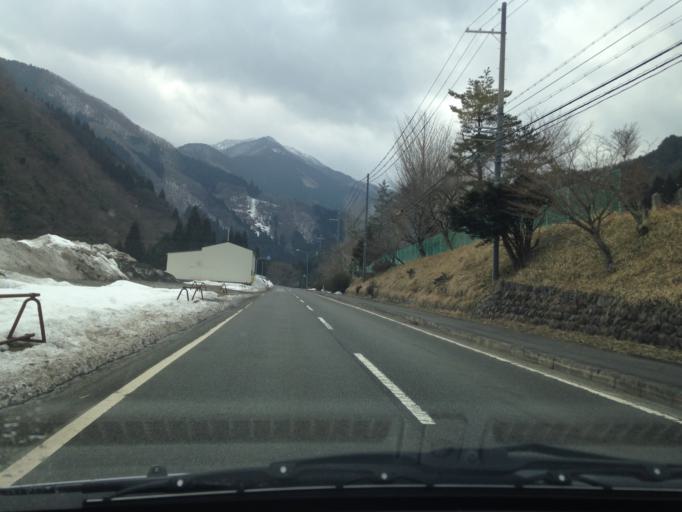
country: JP
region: Hyogo
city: Yamazakicho-nakabirose
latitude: 35.1939
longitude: 134.4478
